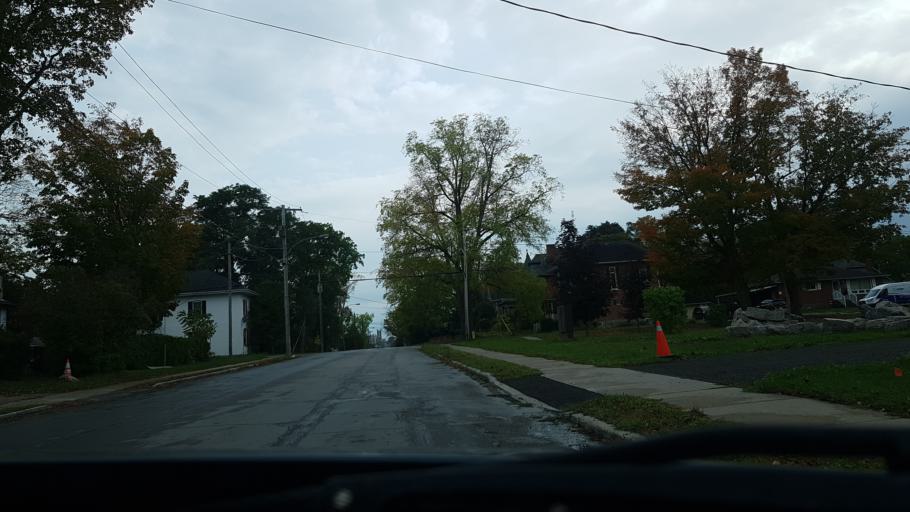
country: CA
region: Ontario
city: Omemee
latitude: 44.3637
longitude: -78.7411
